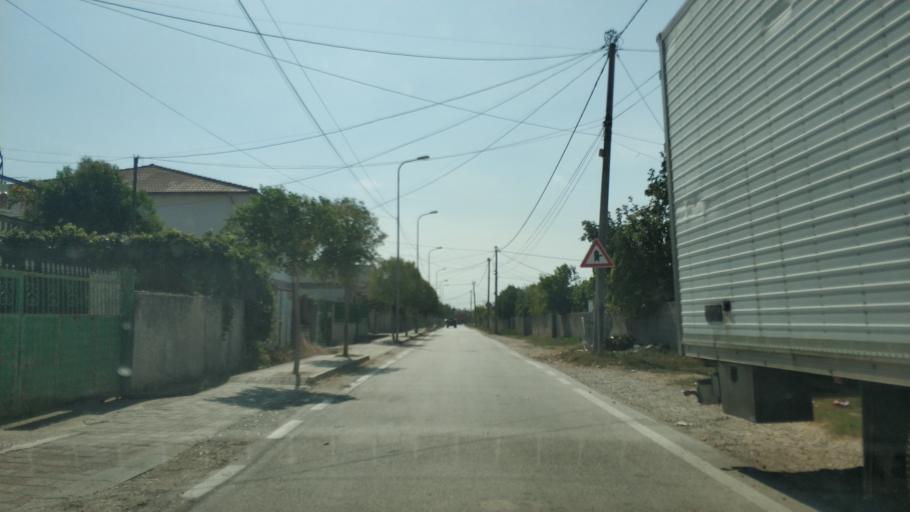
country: AL
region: Fier
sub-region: Rrethi i Fierit
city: Dermenas
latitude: 40.7314
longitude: 19.4696
